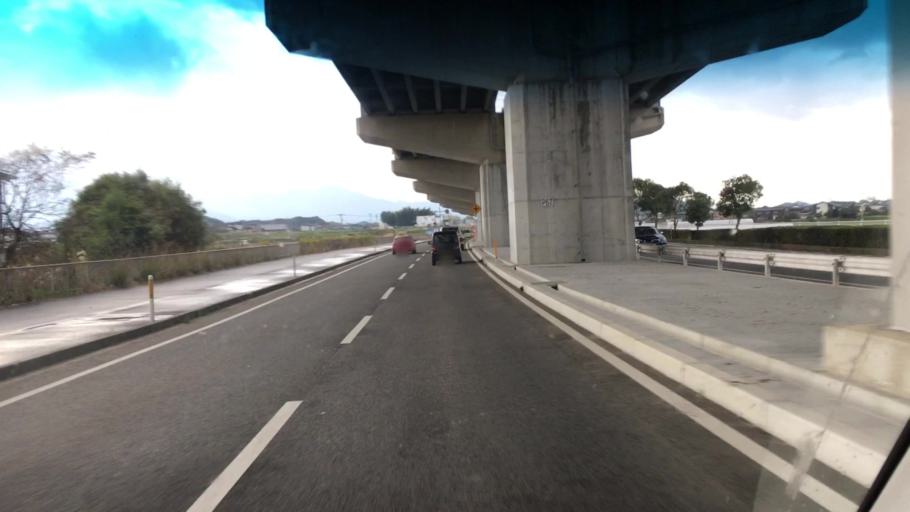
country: JP
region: Fukuoka
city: Maebaru-chuo
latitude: 33.5523
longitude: 130.2219
